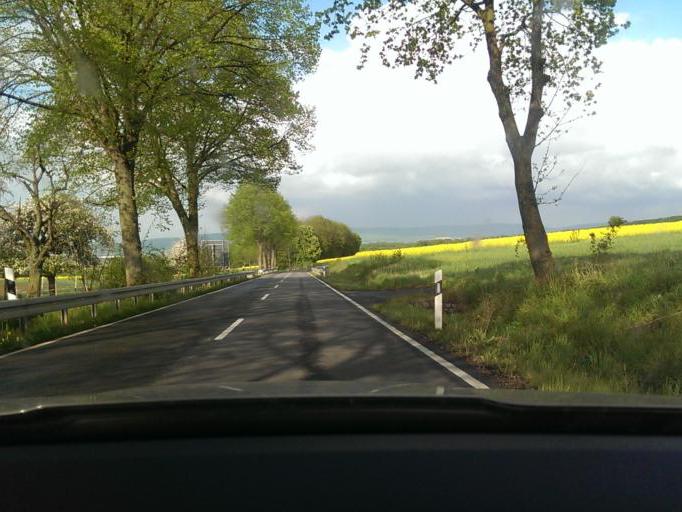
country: DE
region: Lower Saxony
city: Pohle
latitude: 52.2400
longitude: 9.2959
